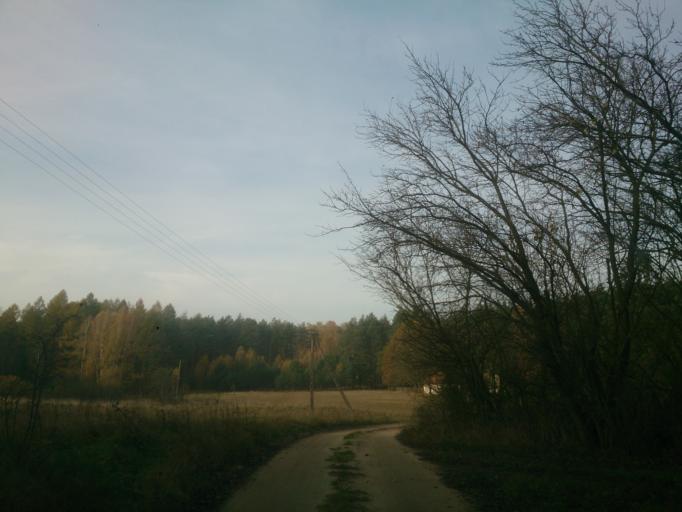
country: PL
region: Kujawsko-Pomorskie
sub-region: Powiat brodnicki
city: Bobrowo
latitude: 53.3728
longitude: 19.3425
